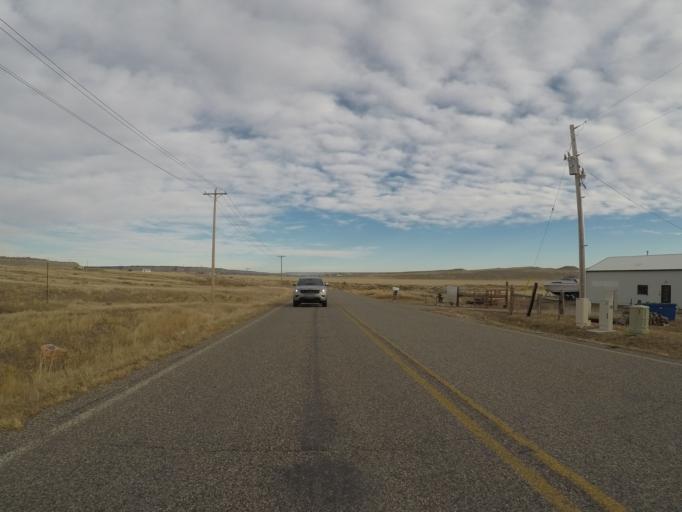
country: US
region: Montana
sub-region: Yellowstone County
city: Laurel
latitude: 45.7814
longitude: -108.7383
